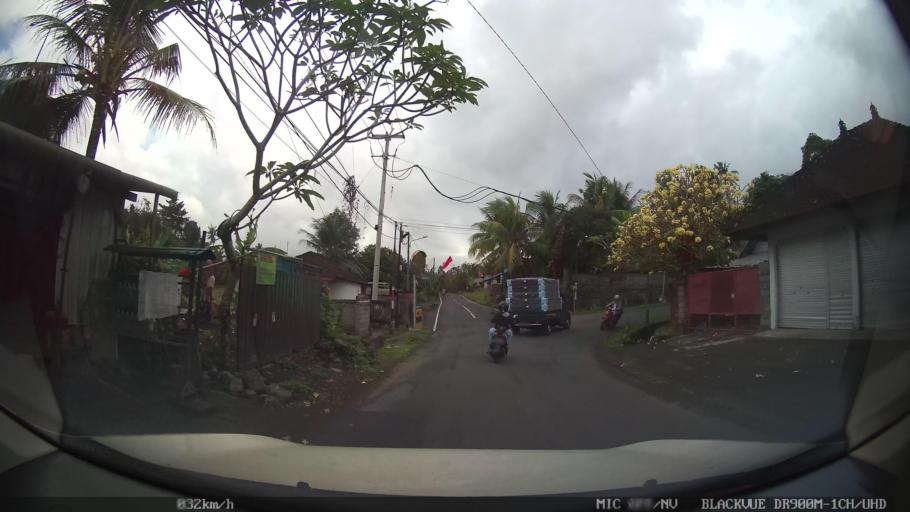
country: ID
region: Bali
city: Banjar Mambalkajanan
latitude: -8.5590
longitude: 115.2080
